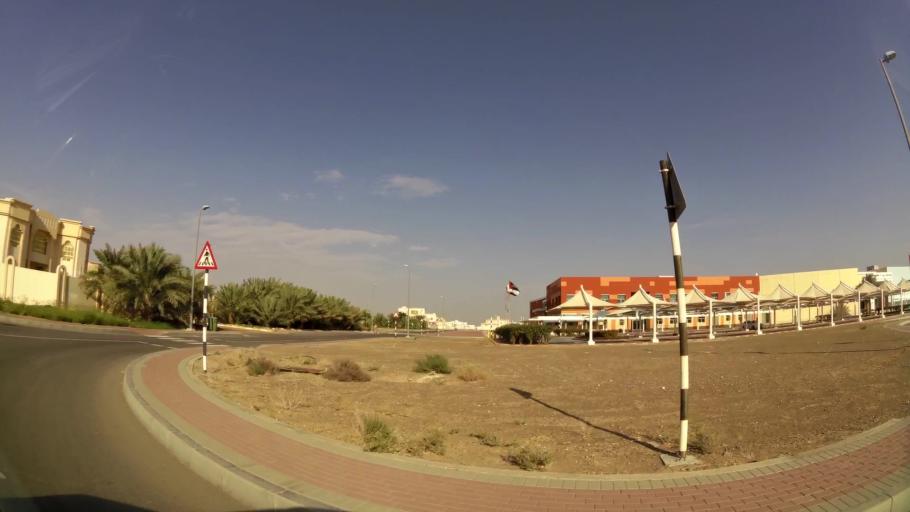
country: AE
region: Abu Dhabi
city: Al Ain
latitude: 24.0487
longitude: 55.8426
